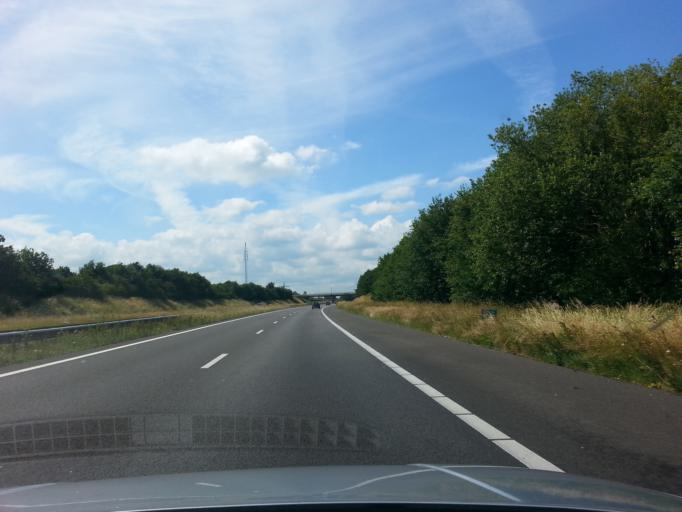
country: NL
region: North Brabant
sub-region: Gemeente Boxmeer
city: Boxmeer
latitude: 51.6107
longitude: 5.9438
